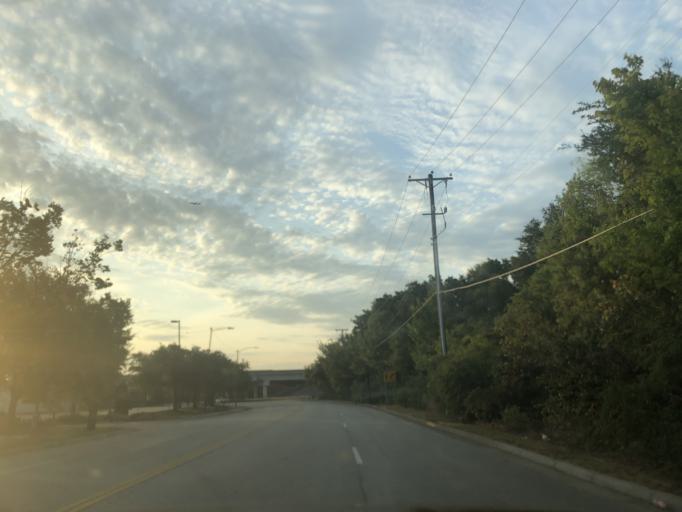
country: US
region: Texas
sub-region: Tarrant County
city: Arlington
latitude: 32.7585
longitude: -97.0781
